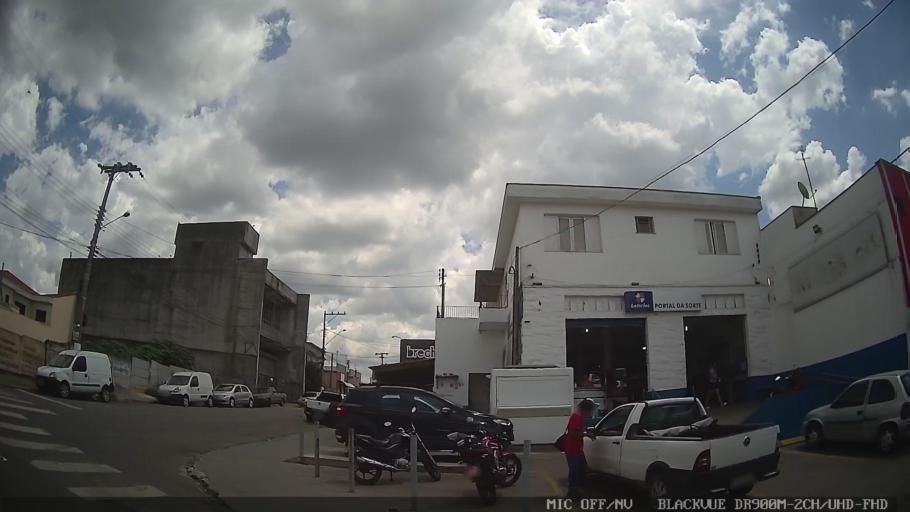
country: BR
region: Sao Paulo
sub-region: Atibaia
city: Atibaia
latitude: -23.1167
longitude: -46.5828
